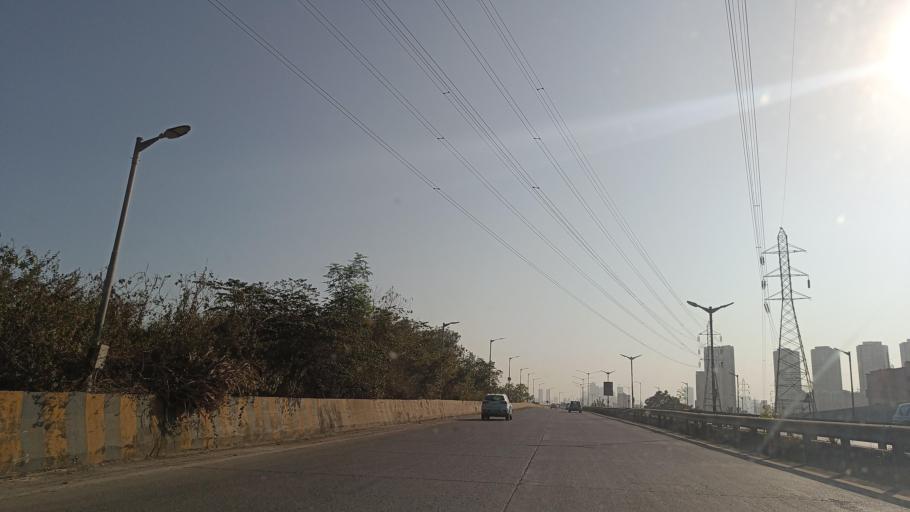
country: IN
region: Maharashtra
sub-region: Mumbai Suburban
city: Mumbai
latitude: 19.0304
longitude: 72.8901
